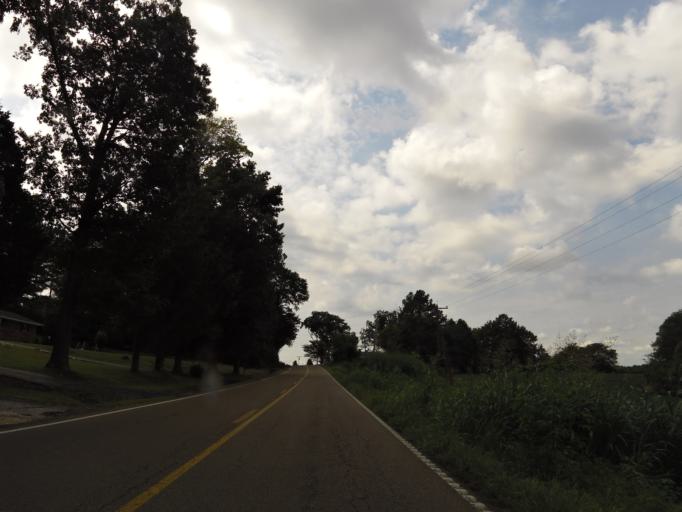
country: US
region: Tennessee
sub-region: Decatur County
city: Decaturville
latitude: 35.5935
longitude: -88.0564
